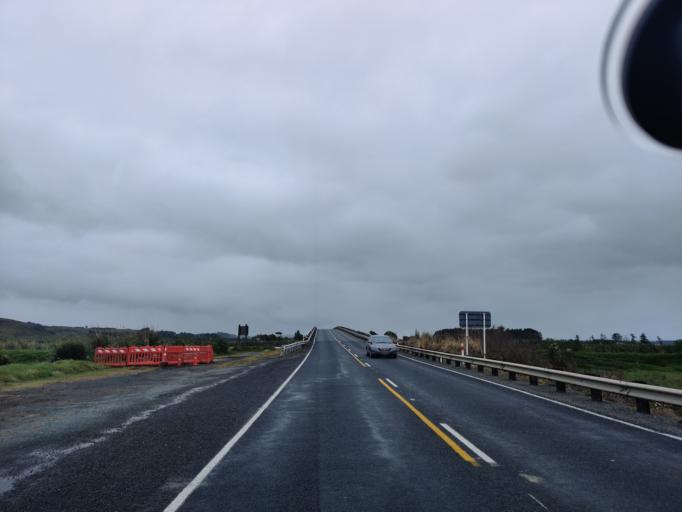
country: NZ
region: Northland
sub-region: Kaipara District
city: Dargaville
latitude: -35.9371
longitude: 173.8824
